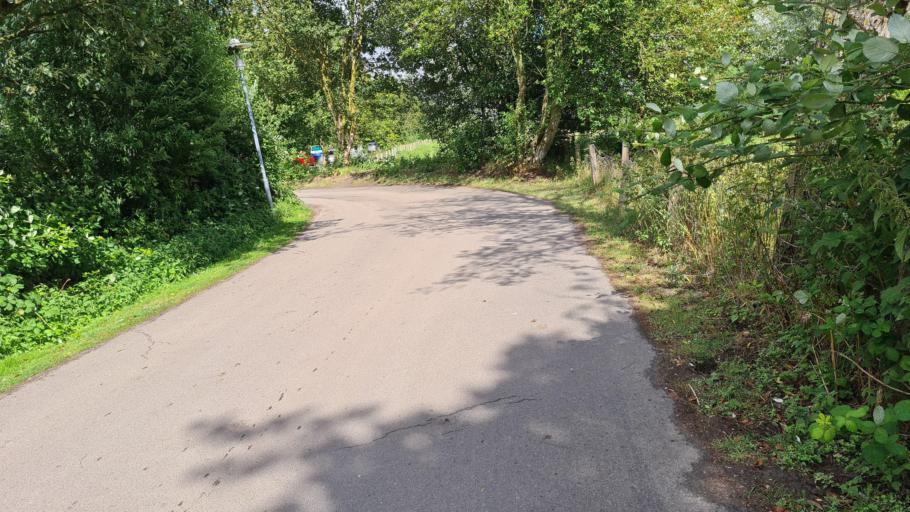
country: DE
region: Schleswig-Holstein
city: Busum
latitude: 54.1301
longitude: 8.8696
